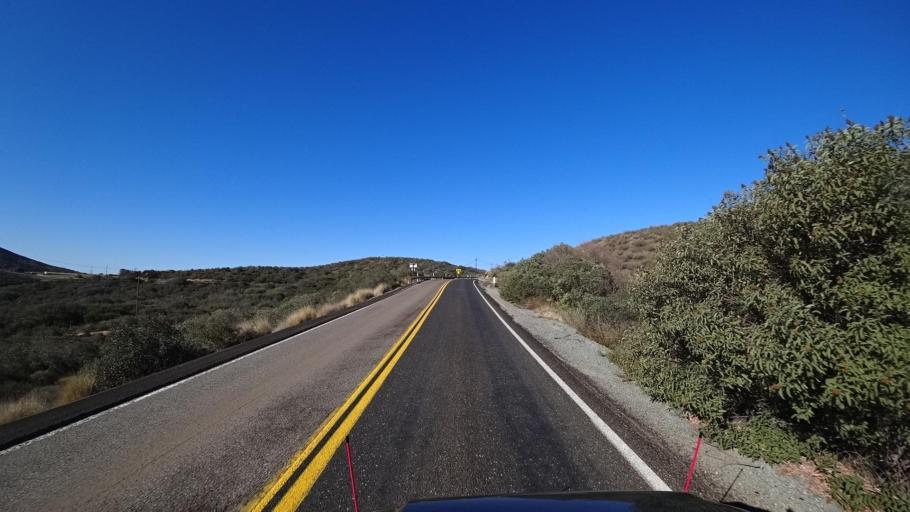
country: MX
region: Baja California
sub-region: Tijuana
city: Villa del Campo
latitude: 32.6168
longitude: -116.7344
